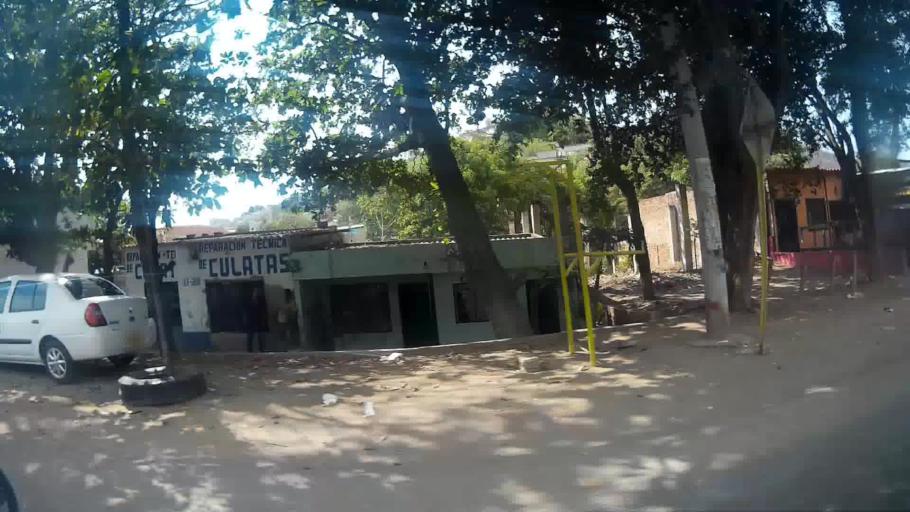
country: CO
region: Magdalena
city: Santa Marta
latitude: 11.1897
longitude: -74.2137
